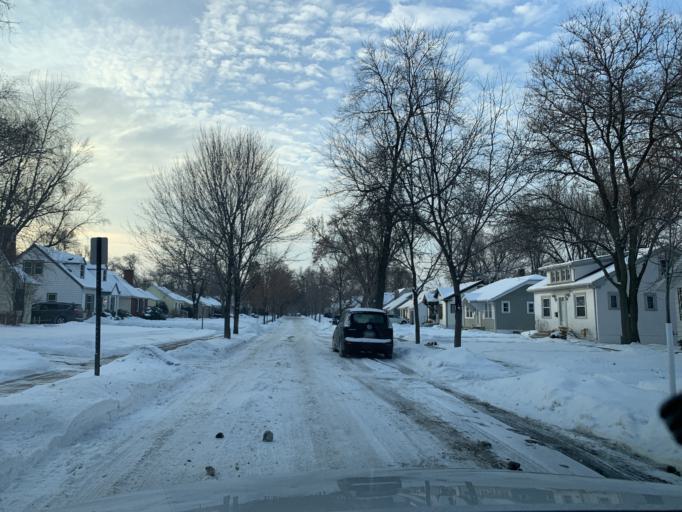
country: US
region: Minnesota
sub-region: Hennepin County
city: Saint Louis Park
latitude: 44.9286
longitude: -93.3520
